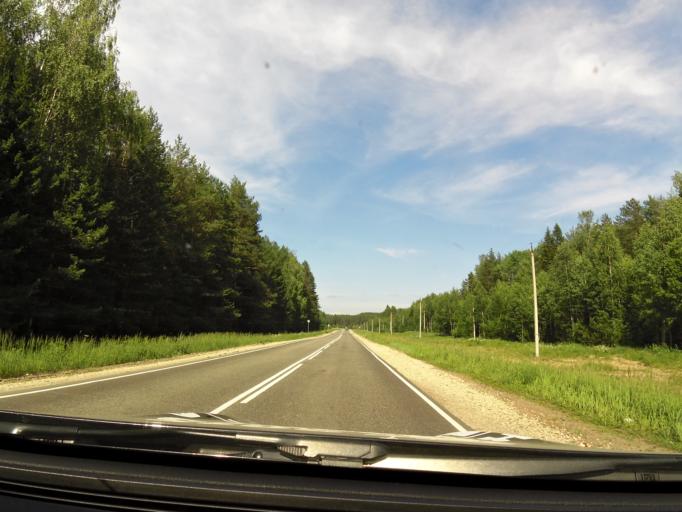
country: RU
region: Kirov
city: Belaya Kholunitsa
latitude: 58.8294
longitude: 50.6803
